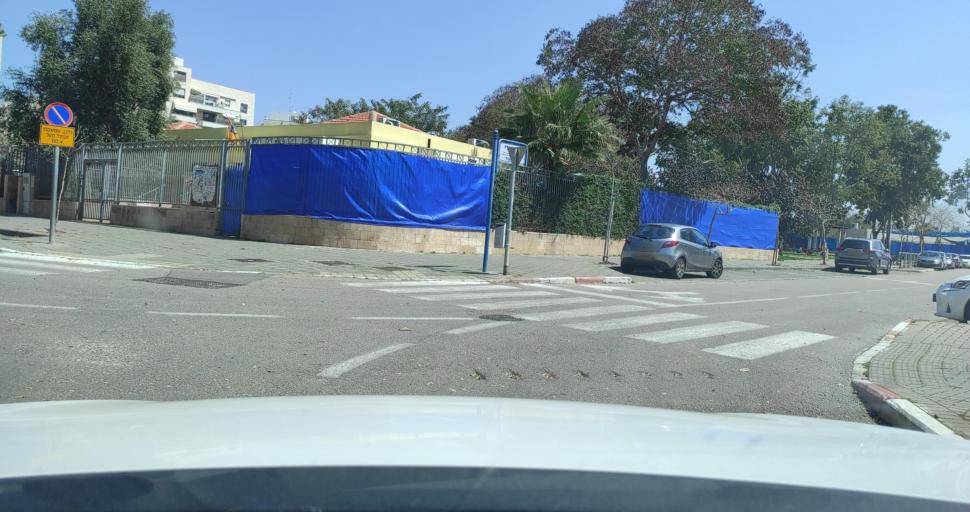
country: IL
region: Central District
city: Nordiyya
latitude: 32.2965
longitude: 34.8706
